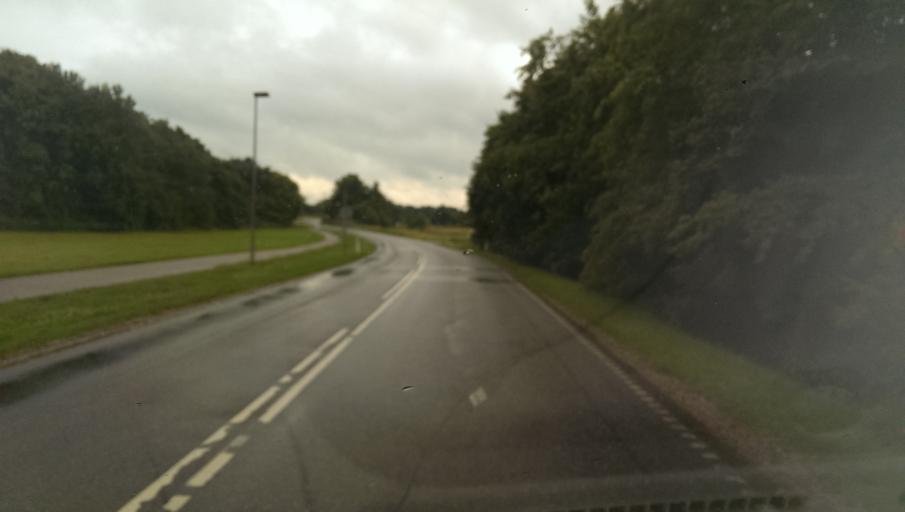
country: DK
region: South Denmark
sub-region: Esbjerg Kommune
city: Bramming
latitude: 55.4844
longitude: 8.6965
